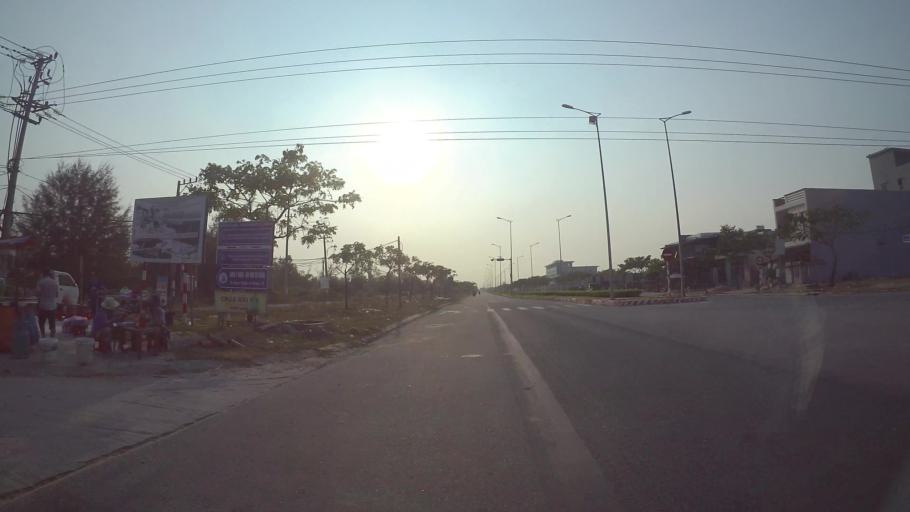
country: VN
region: Da Nang
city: Ngu Hanh Son
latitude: 15.9779
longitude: 108.2502
